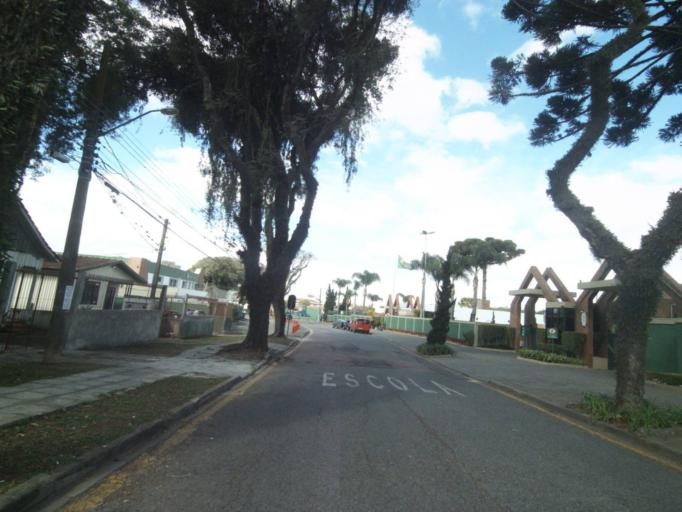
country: BR
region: Parana
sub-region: Curitiba
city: Curitiba
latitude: -25.4566
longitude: -49.2730
